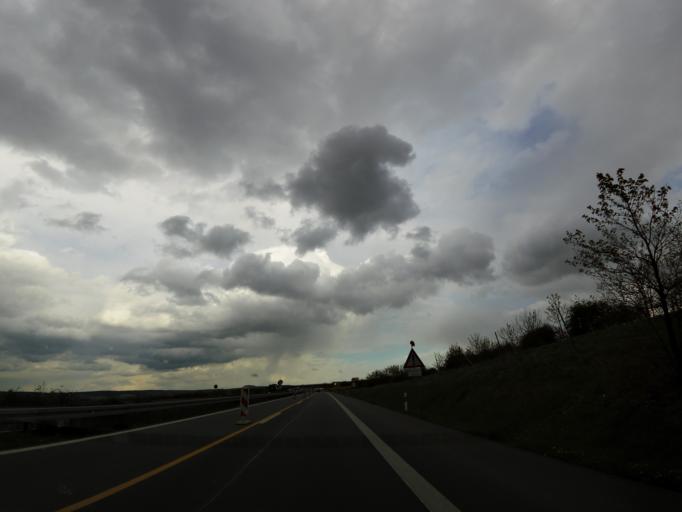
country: DE
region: Saxony-Anhalt
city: Derenburg
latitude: 51.8412
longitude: 10.8629
